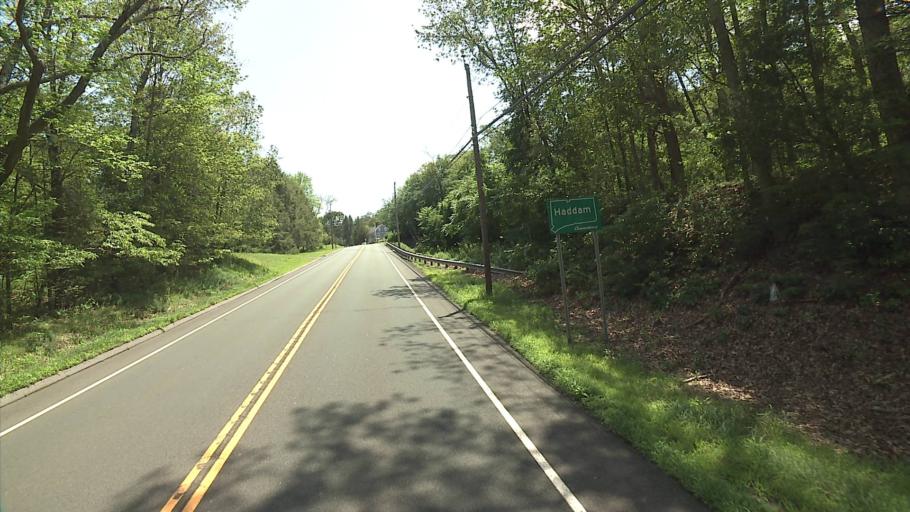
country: US
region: Connecticut
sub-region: Middlesex County
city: Higganum
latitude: 41.4823
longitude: -72.5170
